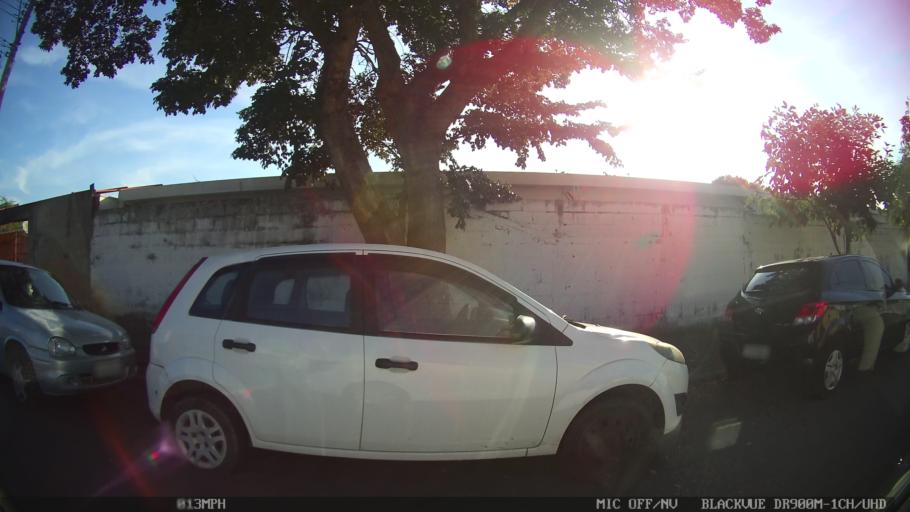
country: BR
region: Sao Paulo
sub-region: Campinas
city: Campinas
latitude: -22.9718
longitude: -47.1245
